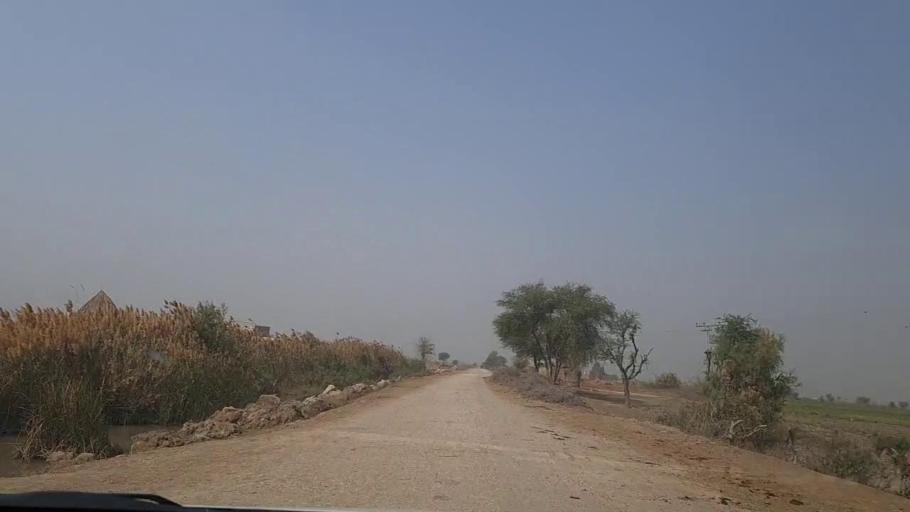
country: PK
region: Sindh
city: Pithoro
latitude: 25.5617
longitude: 69.2087
